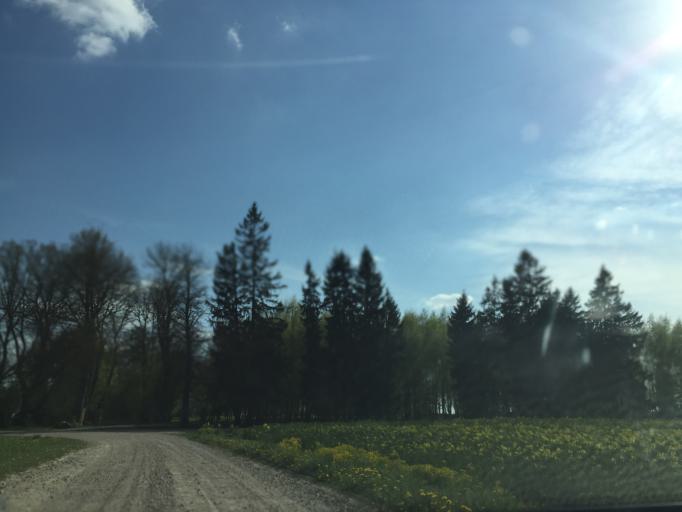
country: LV
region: Bauskas Rajons
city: Bauska
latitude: 56.4914
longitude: 24.3154
